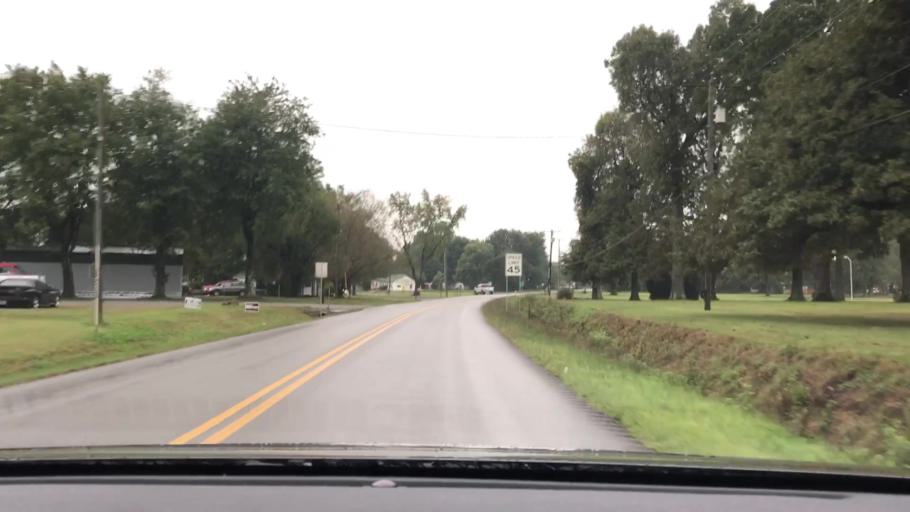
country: US
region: Kentucky
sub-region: Hopkins County
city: Madisonville
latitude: 37.3532
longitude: -87.3940
